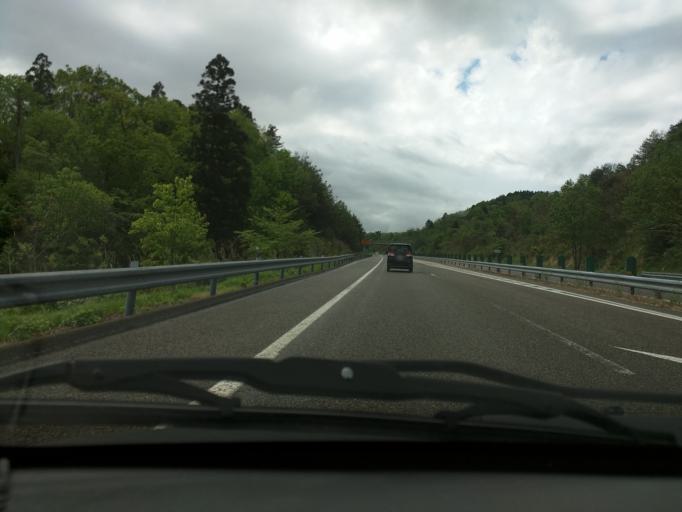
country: JP
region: Niigata
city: Joetsu
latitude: 37.1285
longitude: 138.2128
